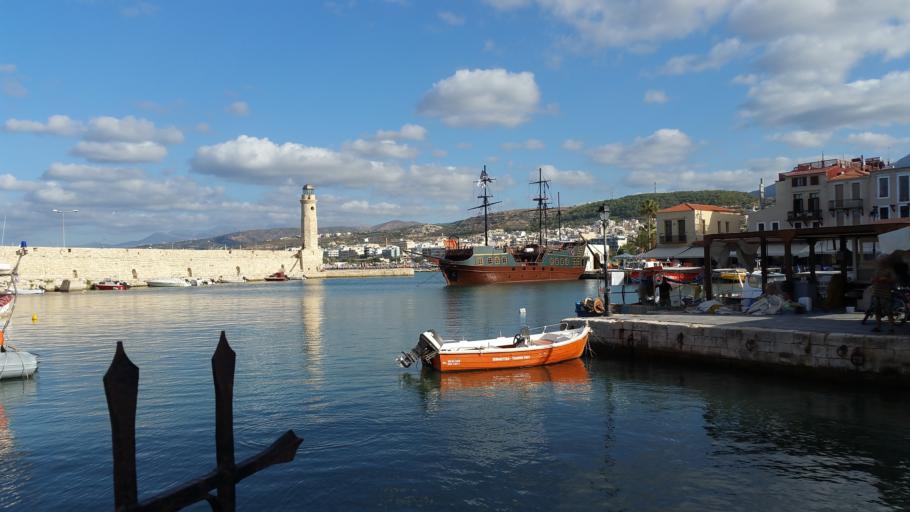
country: GR
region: Crete
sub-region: Nomos Rethymnis
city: Rethymno
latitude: 35.3710
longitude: 24.4761
